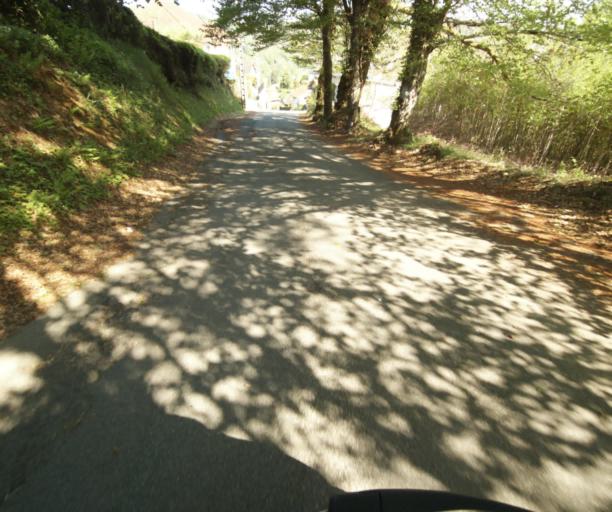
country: FR
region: Limousin
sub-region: Departement de la Correze
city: Tulle
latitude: 45.2671
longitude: 1.7789
